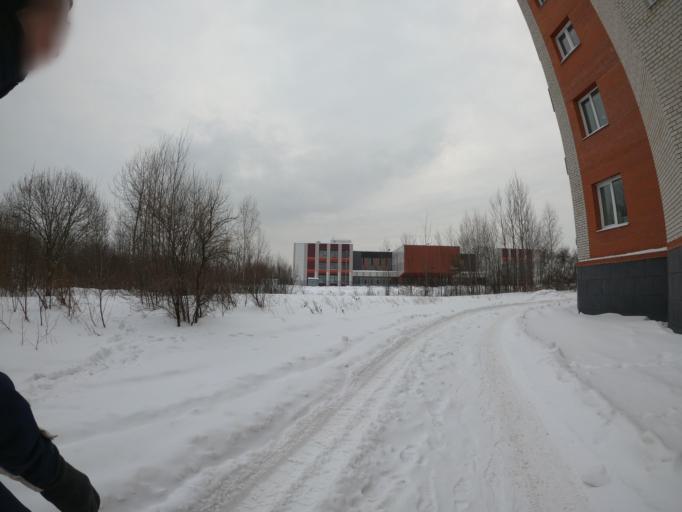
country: RU
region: Moskovskaya
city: Elektrogorsk
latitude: 55.8715
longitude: 38.7783
